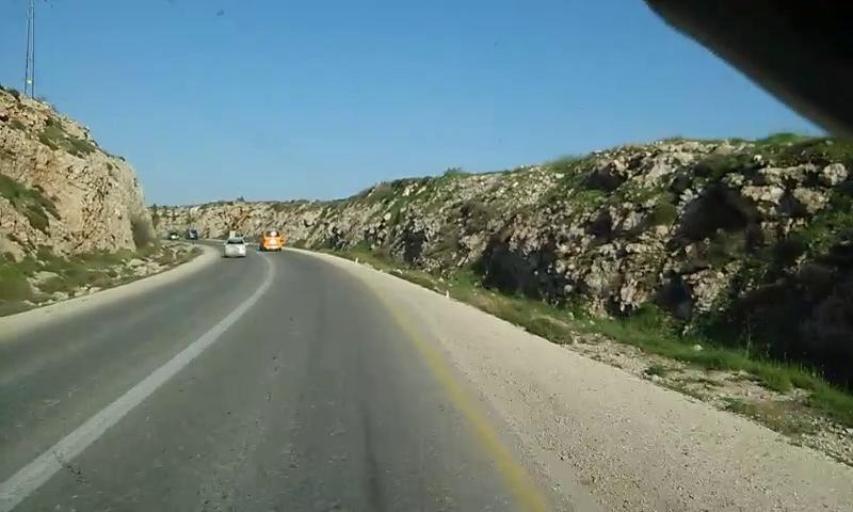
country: PS
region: West Bank
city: Qalqas
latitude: 31.4985
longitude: 35.1031
